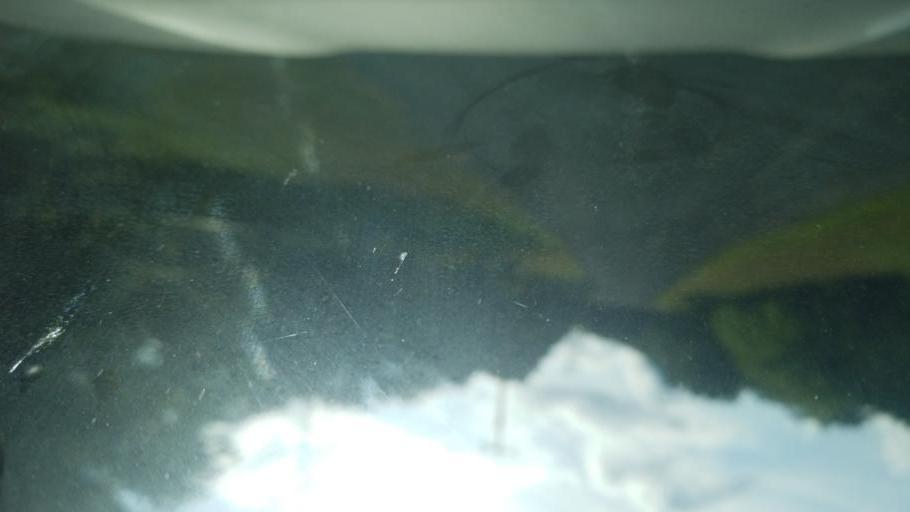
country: US
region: Texas
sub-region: Bexar County
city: Timberwood Park
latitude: 29.6971
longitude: -98.5170
